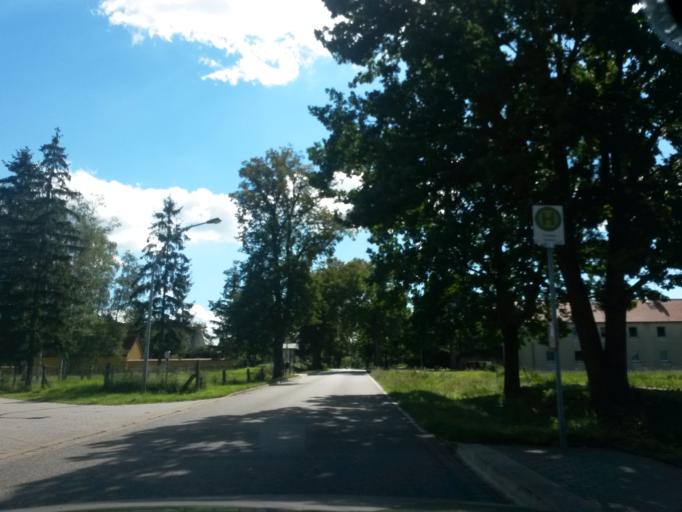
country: DE
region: Brandenburg
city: Schoneberg
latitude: 52.9985
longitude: 14.0856
